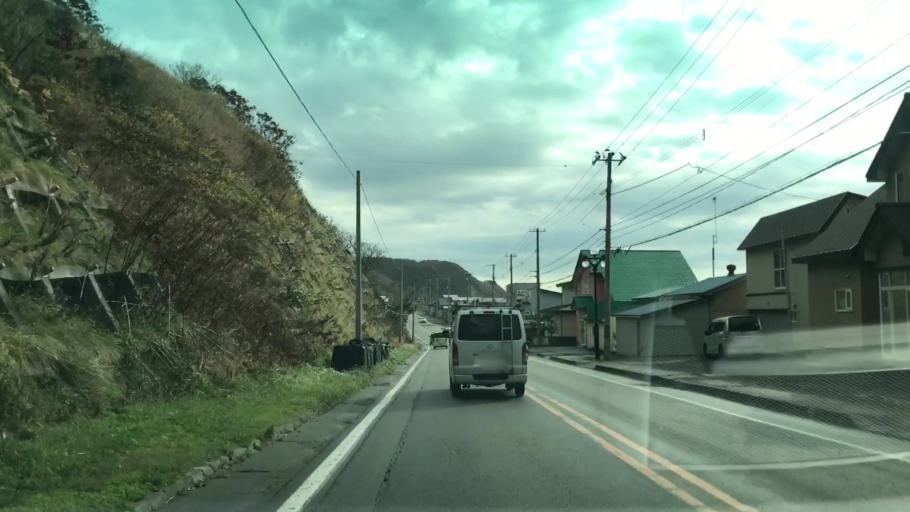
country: JP
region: Hokkaido
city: Shizunai-furukawacho
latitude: 42.1526
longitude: 142.7977
